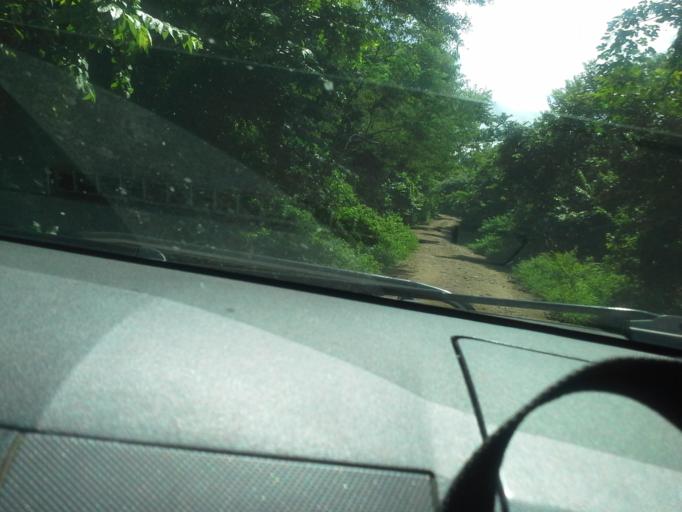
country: NI
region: Matagalpa
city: Terrabona
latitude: 12.7336
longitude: -85.9306
